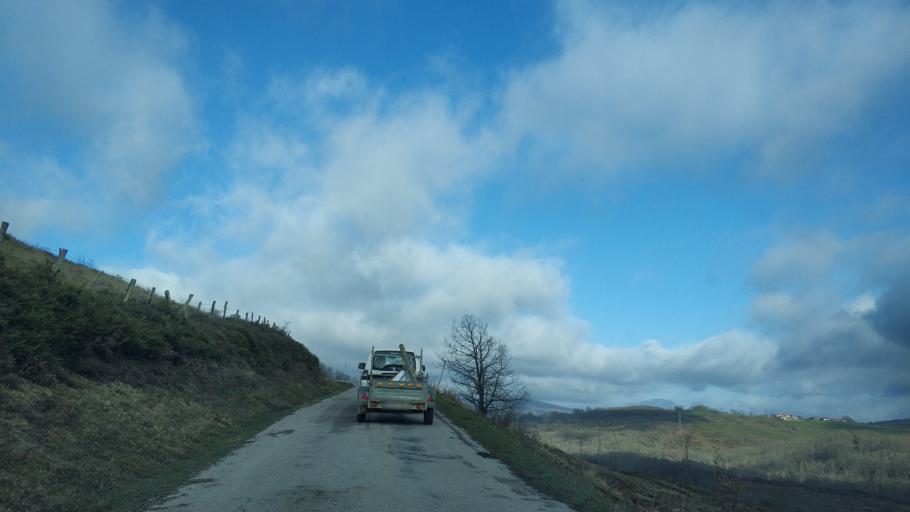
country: ES
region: Castille and Leon
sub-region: Provincia de Burgos
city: Arija
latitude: 42.9100
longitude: -4.0035
